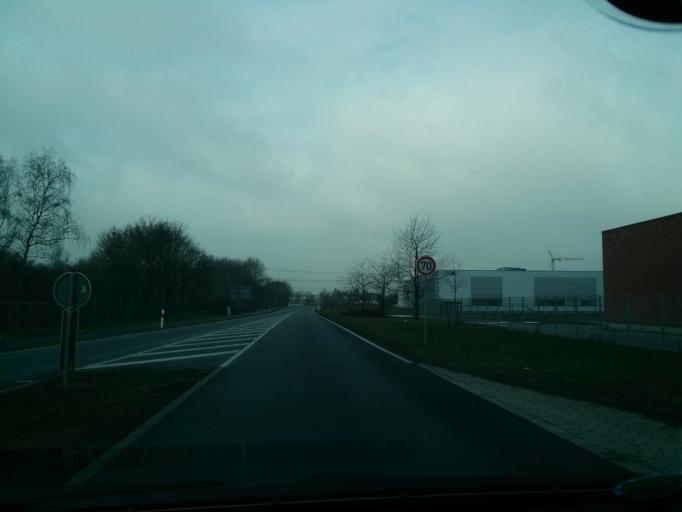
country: DE
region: North Rhine-Westphalia
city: Meckenheim
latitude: 50.6435
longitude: 7.0170
